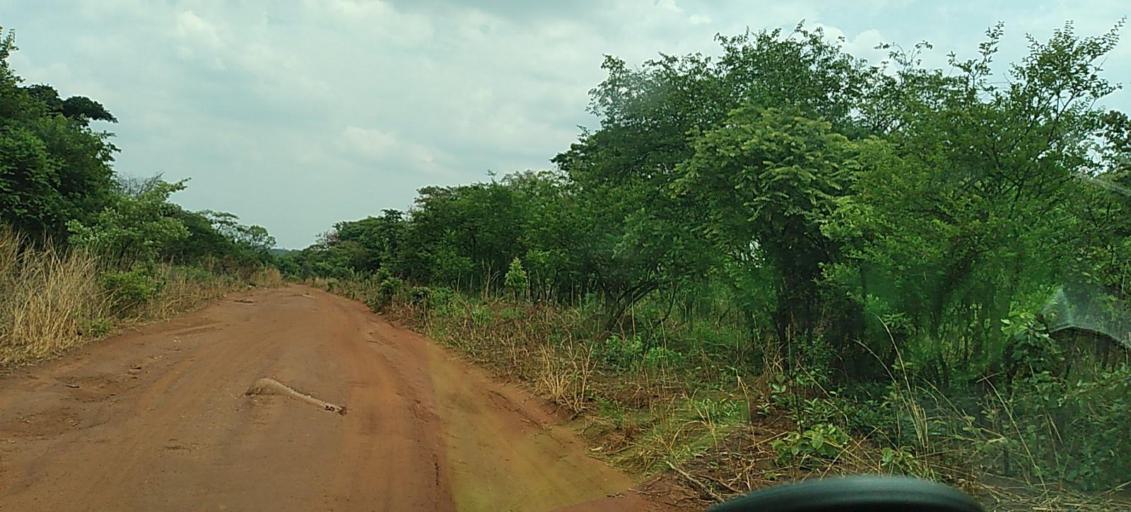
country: ZM
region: North-Western
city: Kansanshi
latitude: -12.0484
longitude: 26.3782
